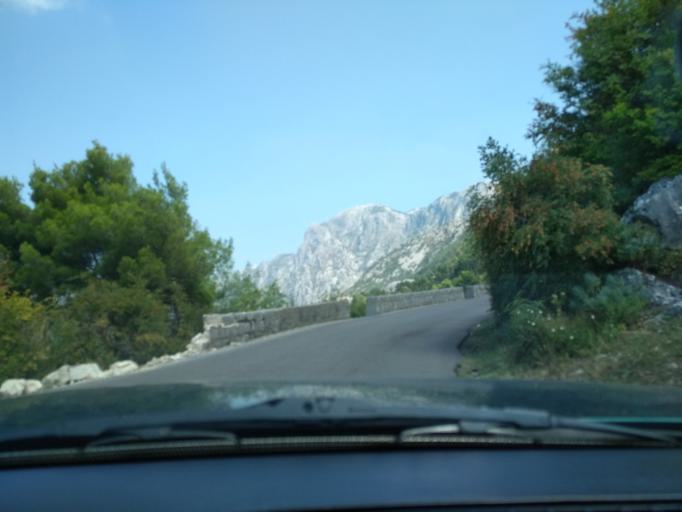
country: ME
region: Kotor
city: Kotor
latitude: 42.4016
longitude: 18.7737
